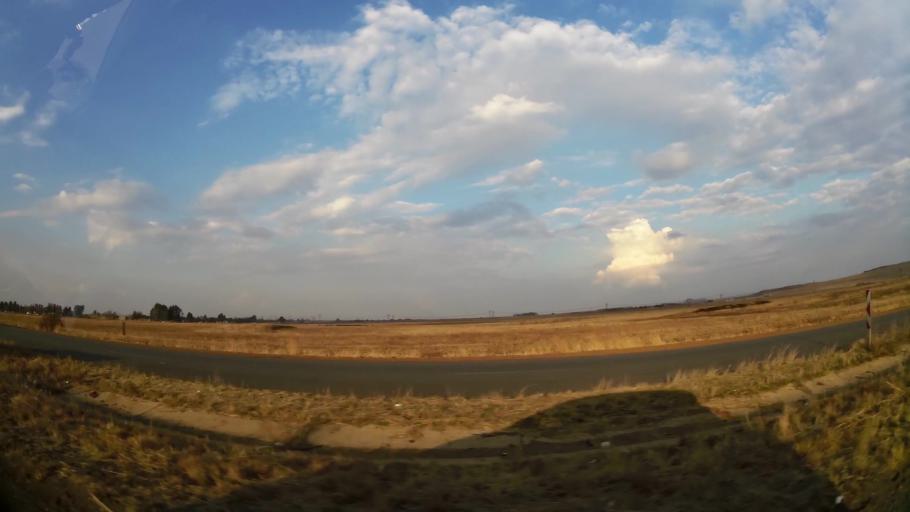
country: ZA
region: Gauteng
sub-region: Sedibeng District Municipality
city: Vanderbijlpark
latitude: -26.6215
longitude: 27.8119
